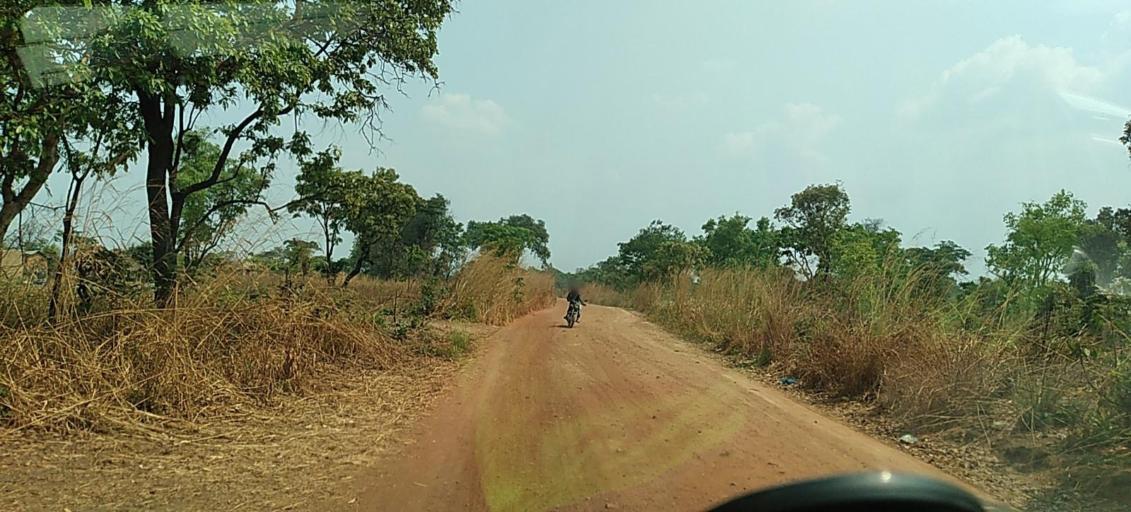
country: ZM
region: North-Western
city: Kansanshi
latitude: -12.0894
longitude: 26.3659
